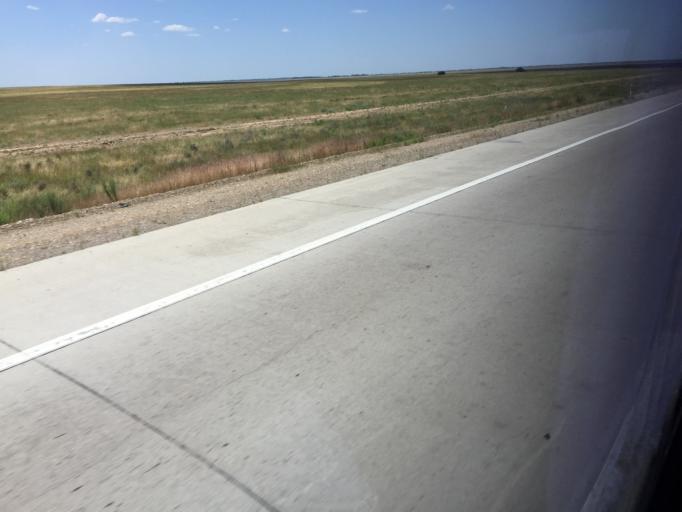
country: KZ
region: Ongtustik Qazaqstan
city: Temirlanovka
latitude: 42.8360
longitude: 69.1157
